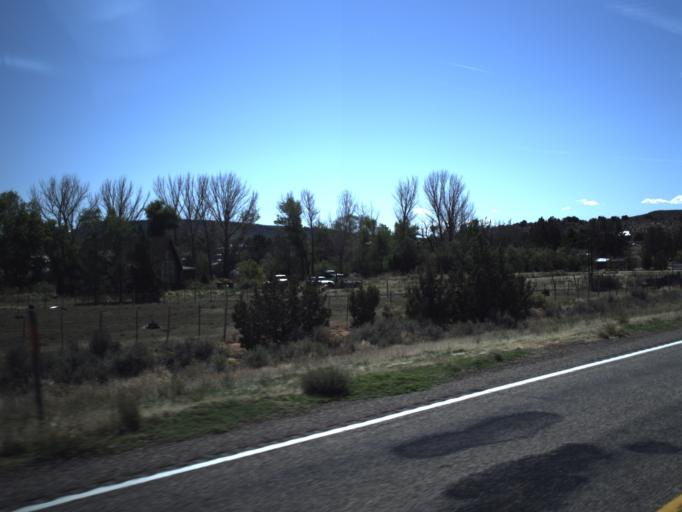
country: US
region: Utah
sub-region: Washington County
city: Ivins
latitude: 37.3641
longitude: -113.6683
